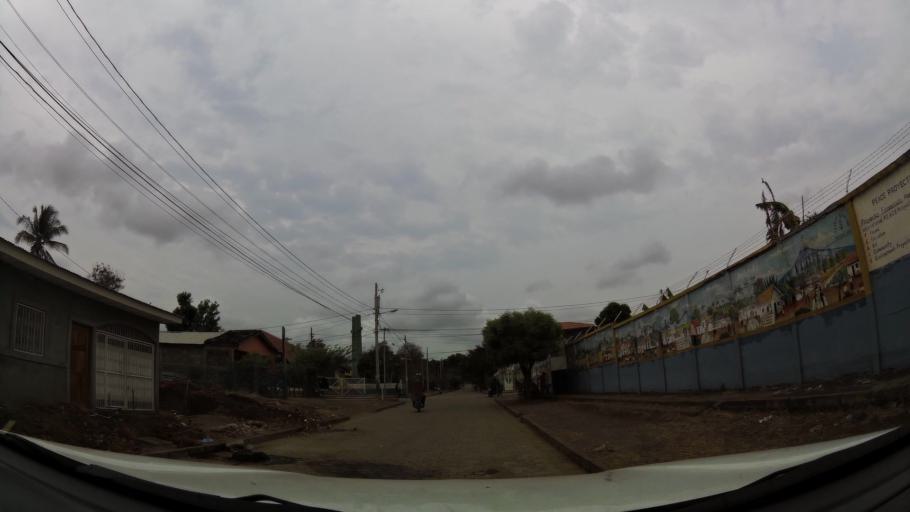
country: NI
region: Granada
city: Granada
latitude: 11.9415
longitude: -85.9579
